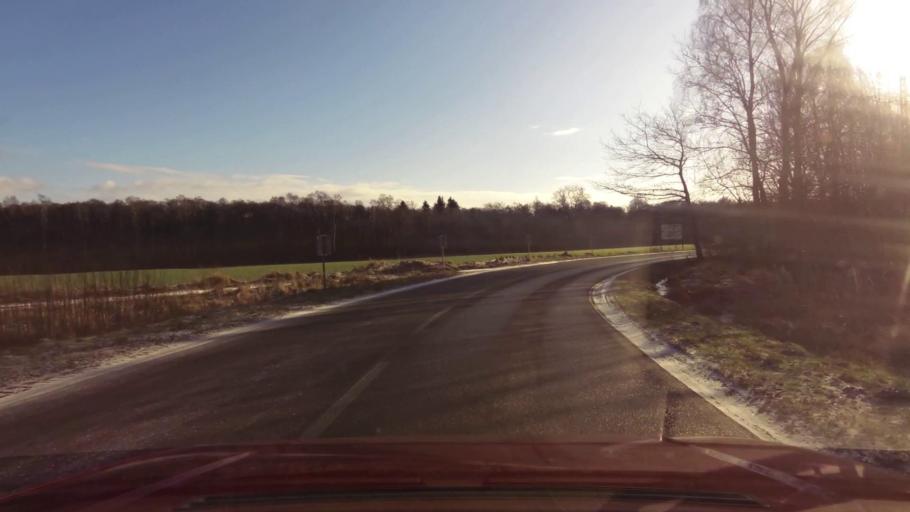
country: PL
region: West Pomeranian Voivodeship
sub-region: Powiat bialogardzki
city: Bialogard
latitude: 54.0273
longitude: 15.9654
